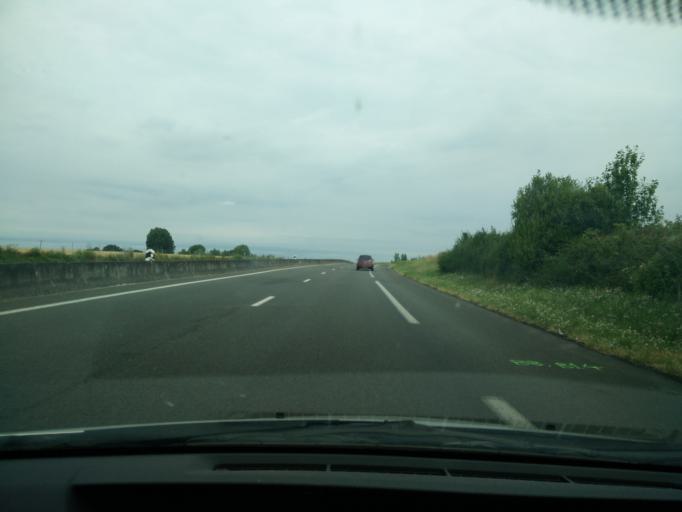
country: FR
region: Pays de la Loire
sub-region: Departement de Maine-et-Loire
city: Saint-Jean
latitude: 47.2485
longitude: -0.3257
